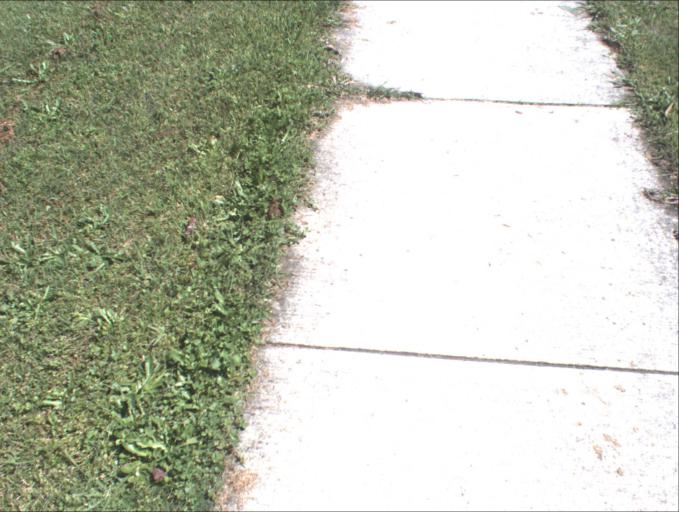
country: AU
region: Queensland
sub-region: Logan
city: North Maclean
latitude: -27.7489
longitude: 153.0247
